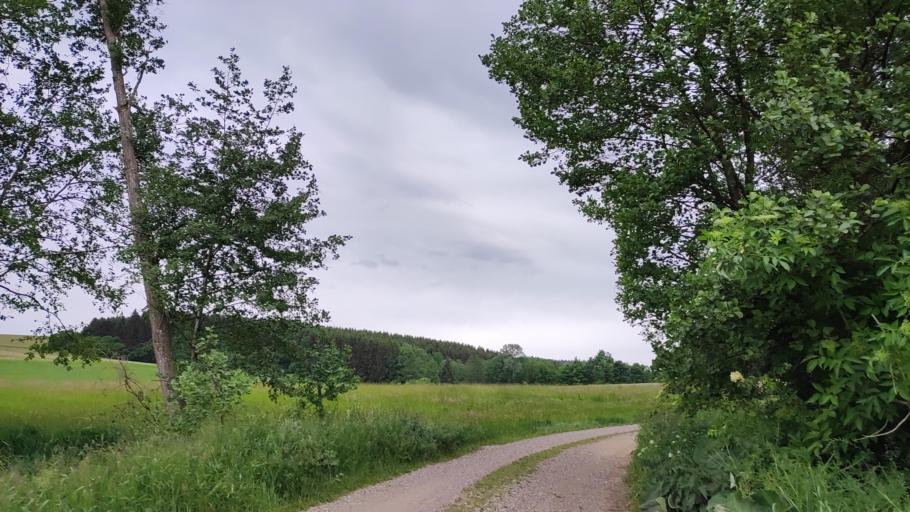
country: DE
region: Bavaria
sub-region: Swabia
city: Dinkelscherben
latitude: 48.3580
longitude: 10.5517
